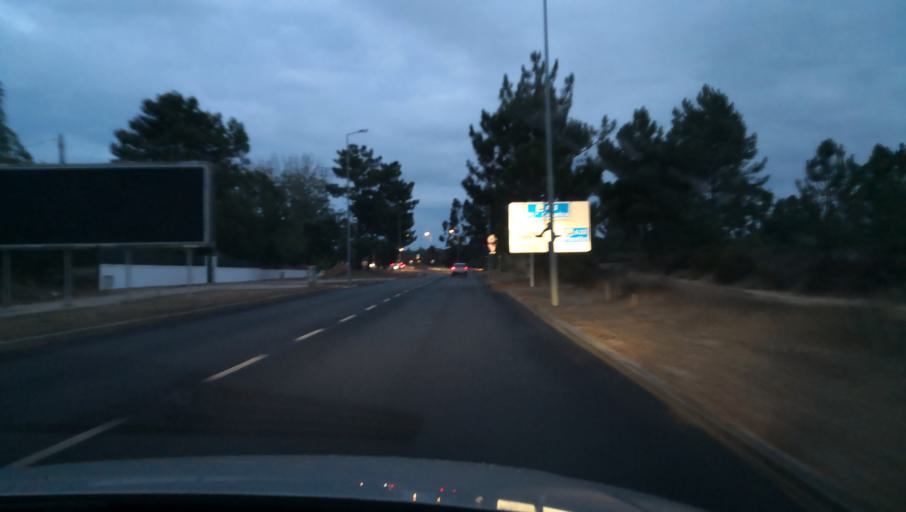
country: PT
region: Setubal
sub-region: Seixal
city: Amora
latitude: 38.6045
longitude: -9.1321
